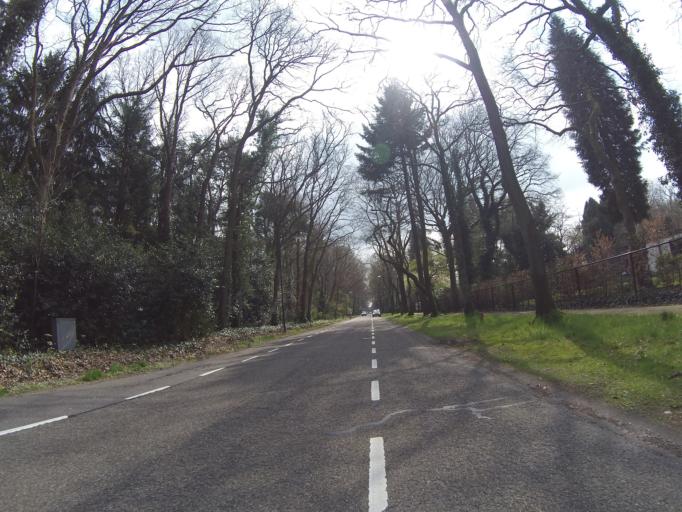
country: NL
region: Utrecht
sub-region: Gemeente Soest
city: Soest
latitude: 52.1210
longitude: 5.2915
